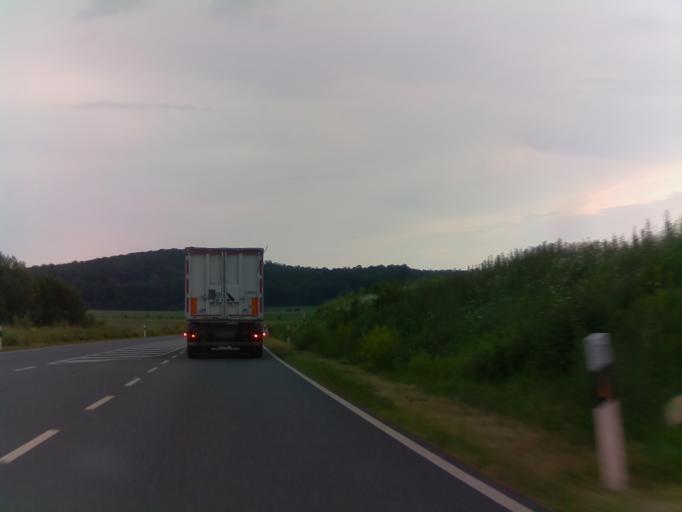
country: DE
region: Lower Saxony
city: Elze
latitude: 52.1153
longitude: 9.6843
